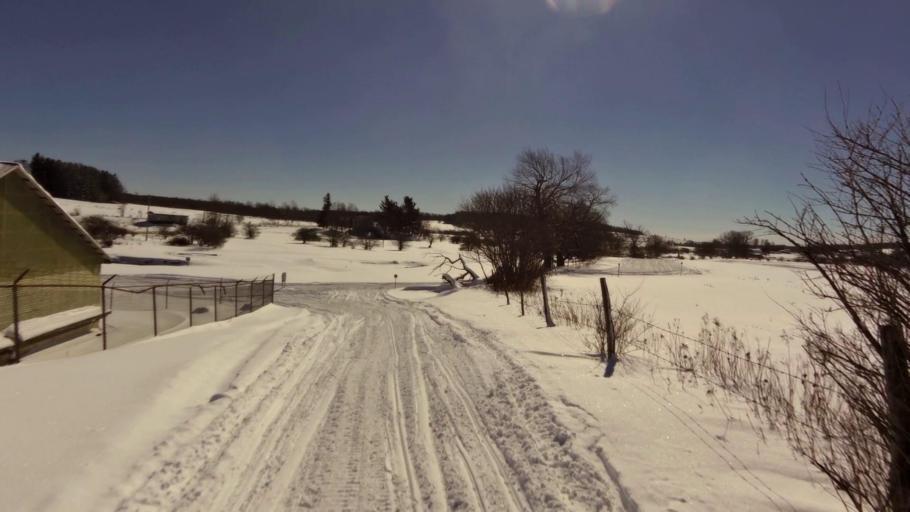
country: US
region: New York
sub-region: Chautauqua County
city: Mayville
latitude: 42.1561
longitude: -79.6009
